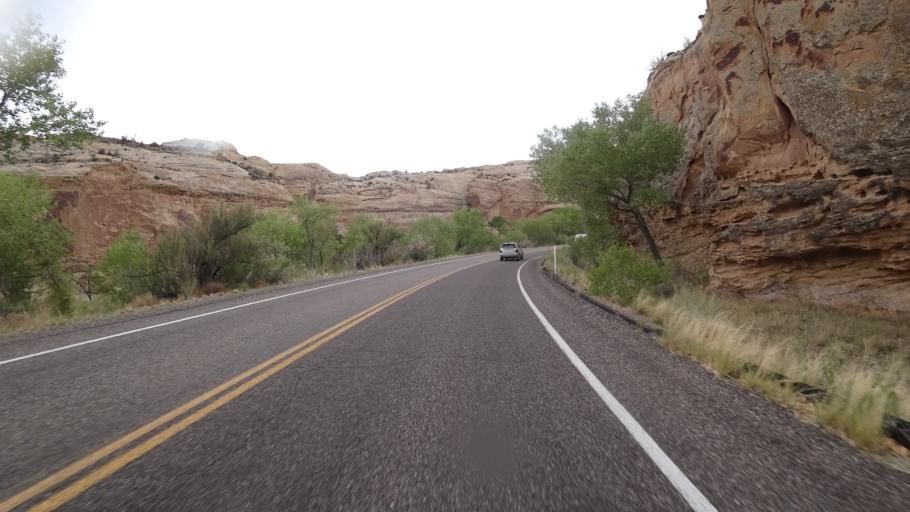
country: US
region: Utah
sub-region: Wayne County
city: Loa
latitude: 38.2851
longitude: -111.1957
